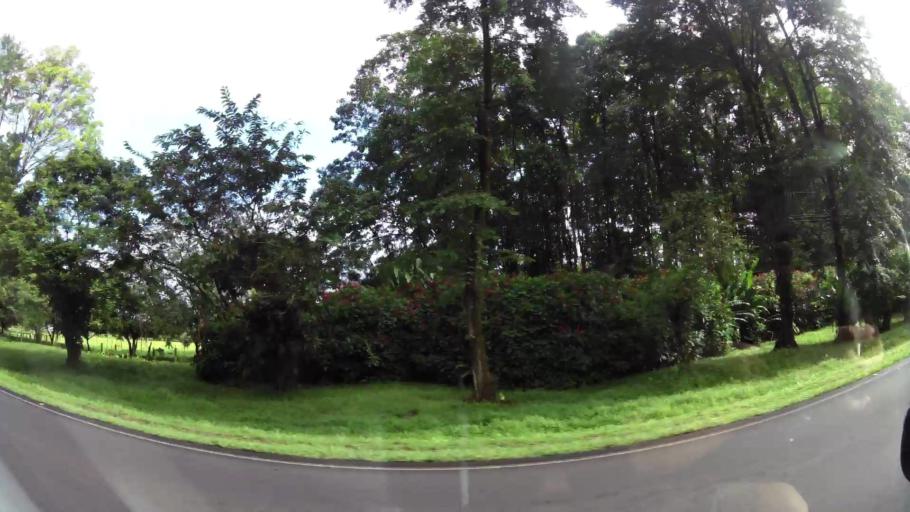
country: CR
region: Limon
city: Pocora
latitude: 10.1895
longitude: -83.6362
